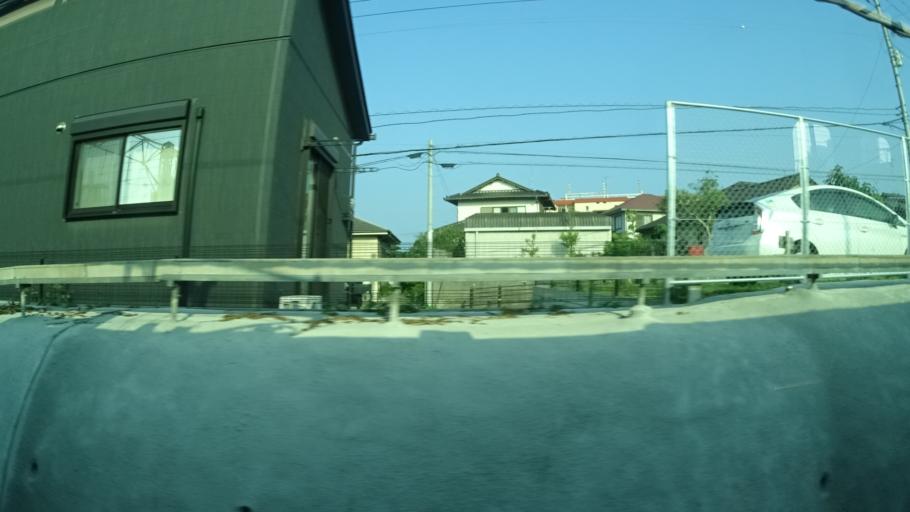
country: JP
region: Ibaraki
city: Hitachi
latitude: 36.5929
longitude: 140.6634
